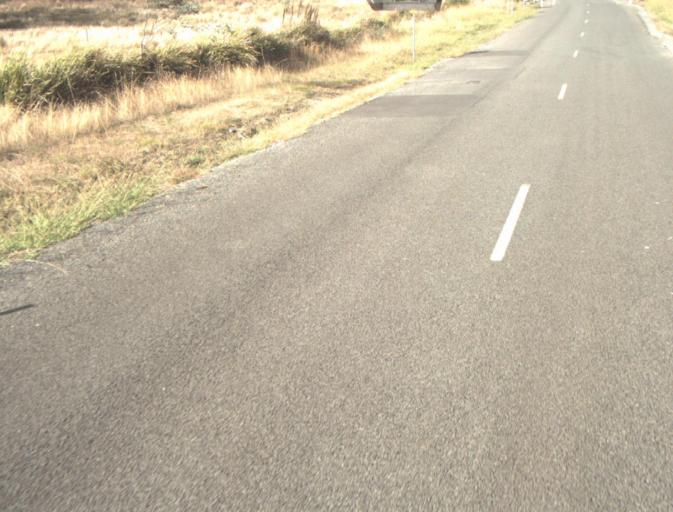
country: AU
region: Tasmania
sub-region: Launceston
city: Mayfield
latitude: -41.2095
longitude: 147.1243
